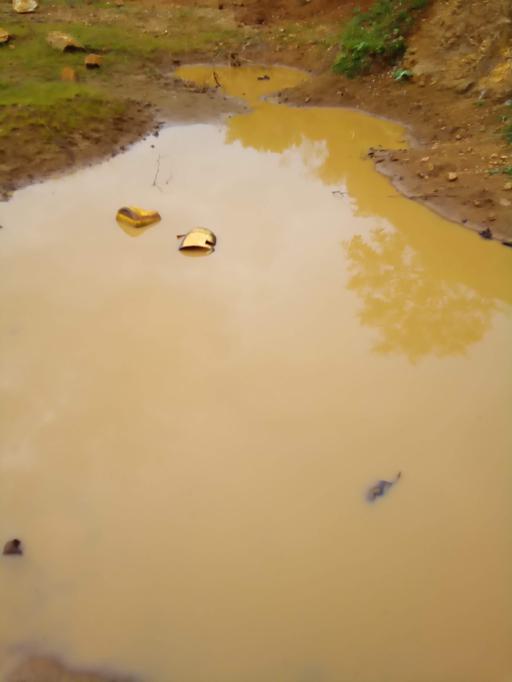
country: KE
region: Homa Bay
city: Homa Bay
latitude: -0.4892
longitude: 34.1749
